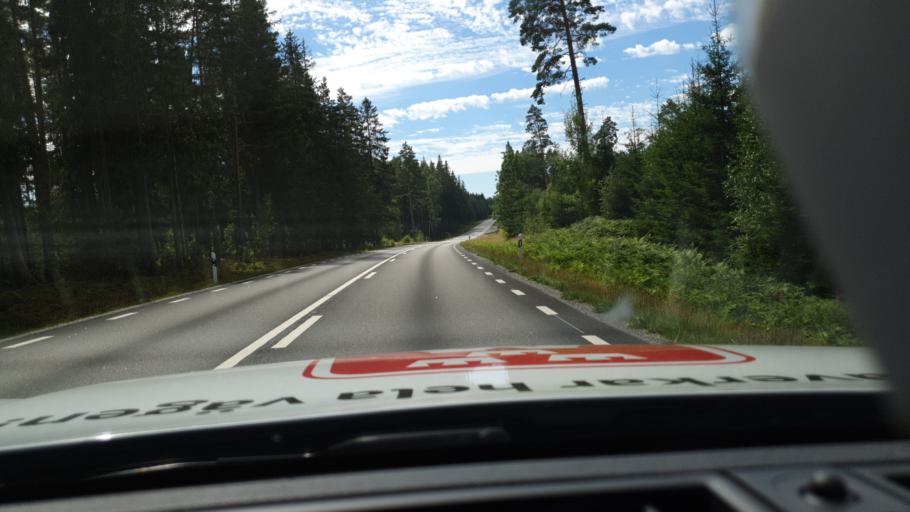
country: SE
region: Joenkoeping
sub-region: Savsjo Kommun
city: Stockaryd
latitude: 57.2875
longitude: 14.5234
